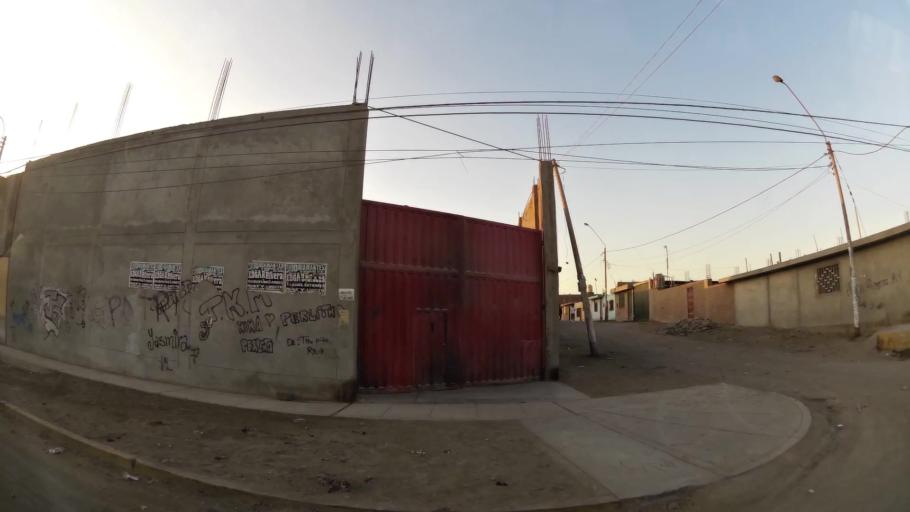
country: PE
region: Ica
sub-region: Provincia de Pisco
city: San Clemente
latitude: -13.6781
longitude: -76.1520
